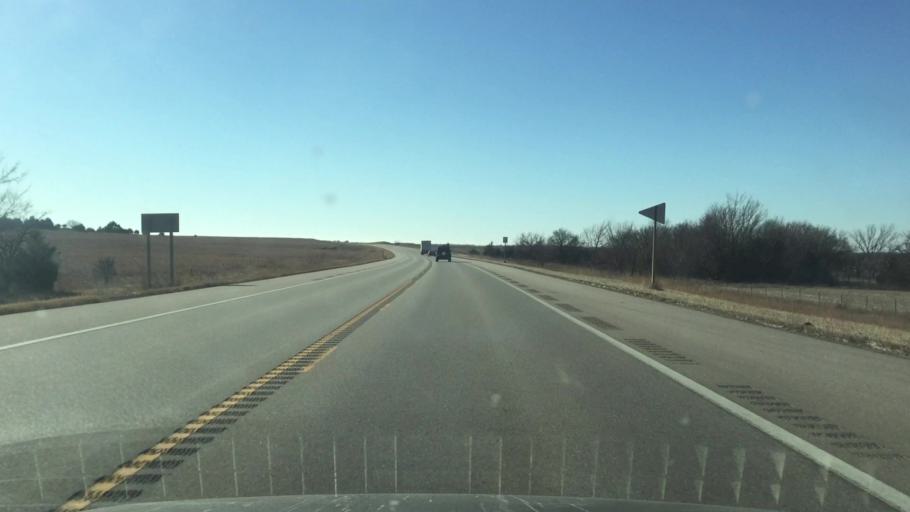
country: US
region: Kansas
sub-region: Allen County
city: Iola
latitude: 38.0663
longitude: -95.3796
